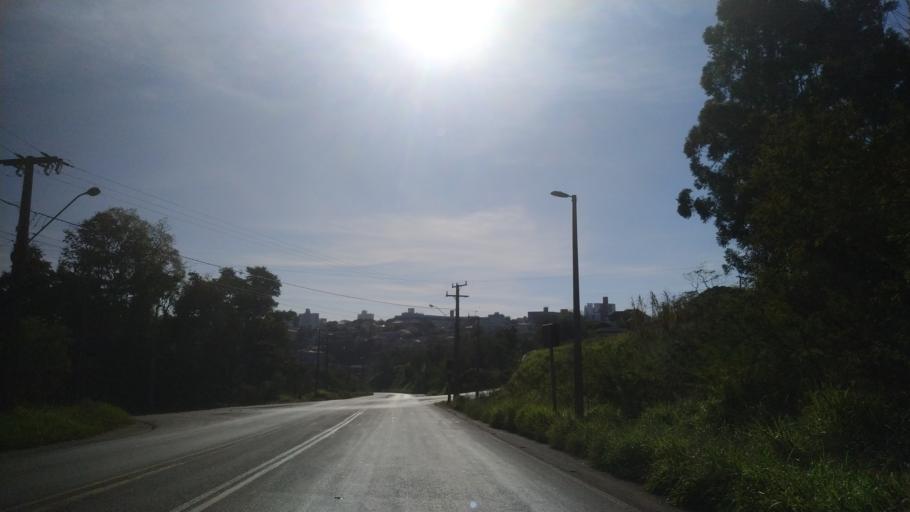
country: BR
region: Santa Catarina
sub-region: Chapeco
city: Chapeco
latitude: -27.1147
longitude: -52.6306
